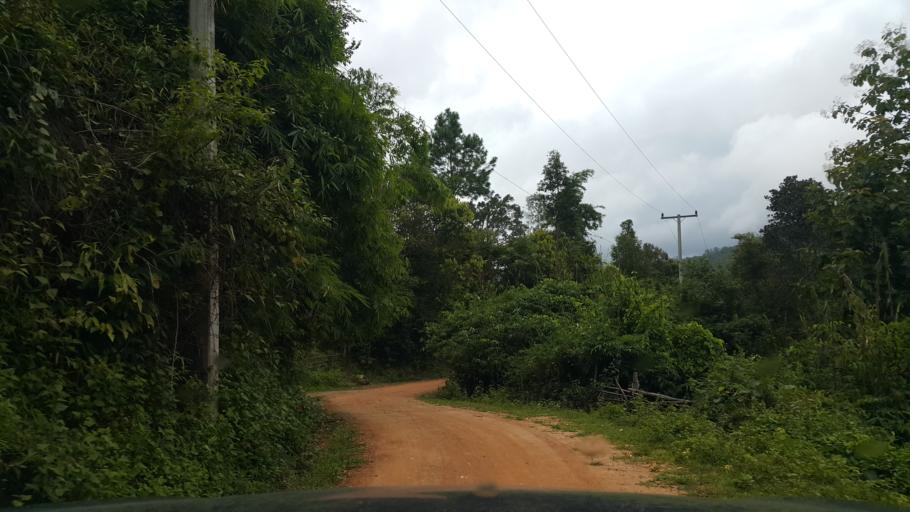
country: TH
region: Chiang Mai
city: Samoeng
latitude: 18.8145
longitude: 98.6254
